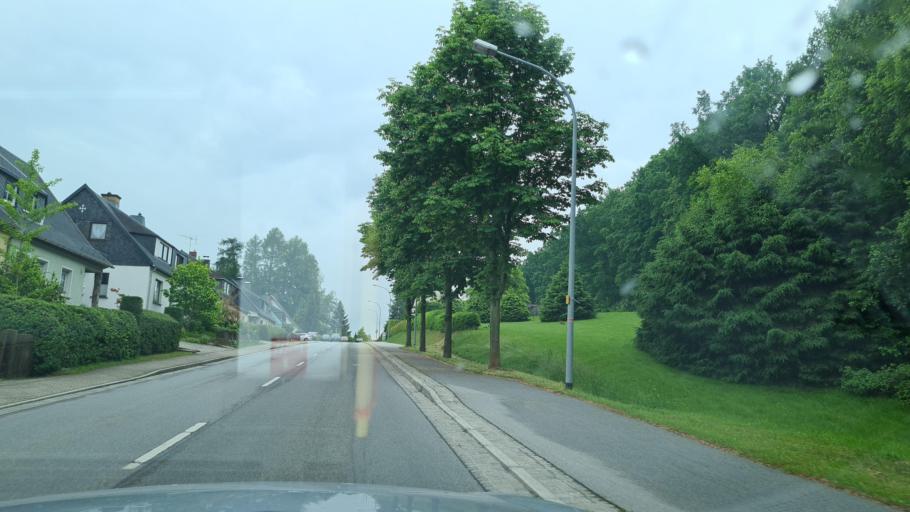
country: DE
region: Saxony
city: Schirgiswalde
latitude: 51.0703
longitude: 14.4286
